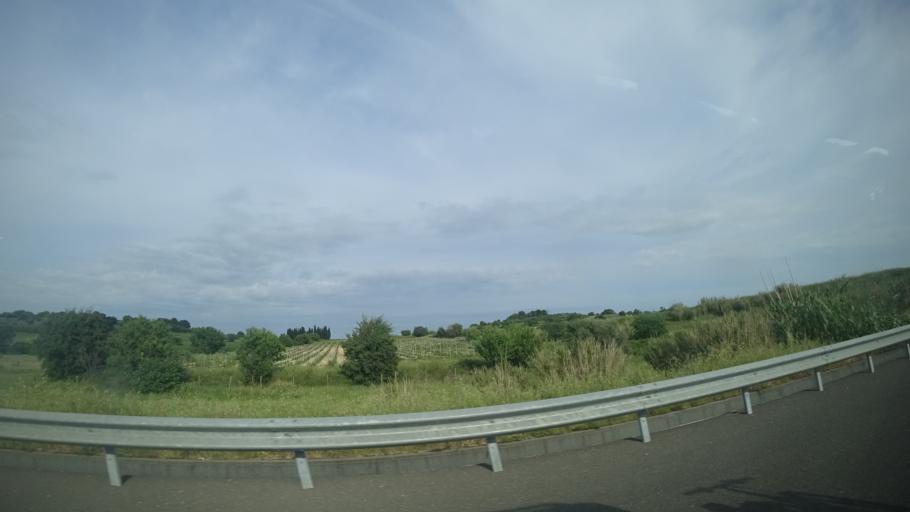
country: FR
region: Languedoc-Roussillon
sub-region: Departement de l'Herault
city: Tourbes
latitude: 43.4288
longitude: 3.3906
